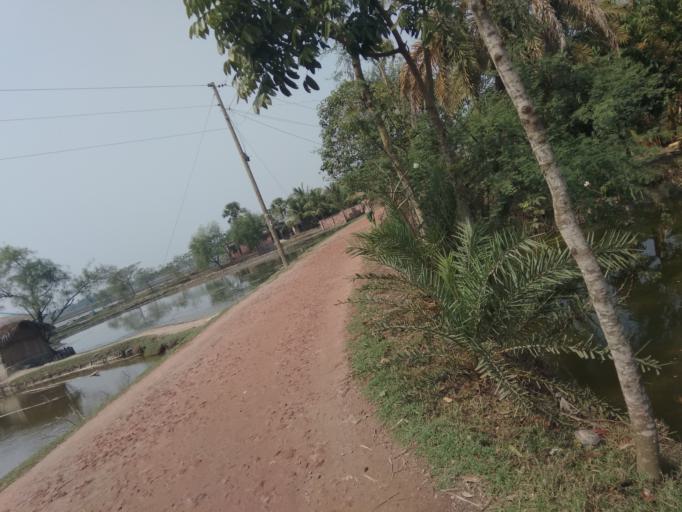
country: IN
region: West Bengal
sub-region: North 24 Parganas
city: Taki
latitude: 22.3004
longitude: 89.2685
